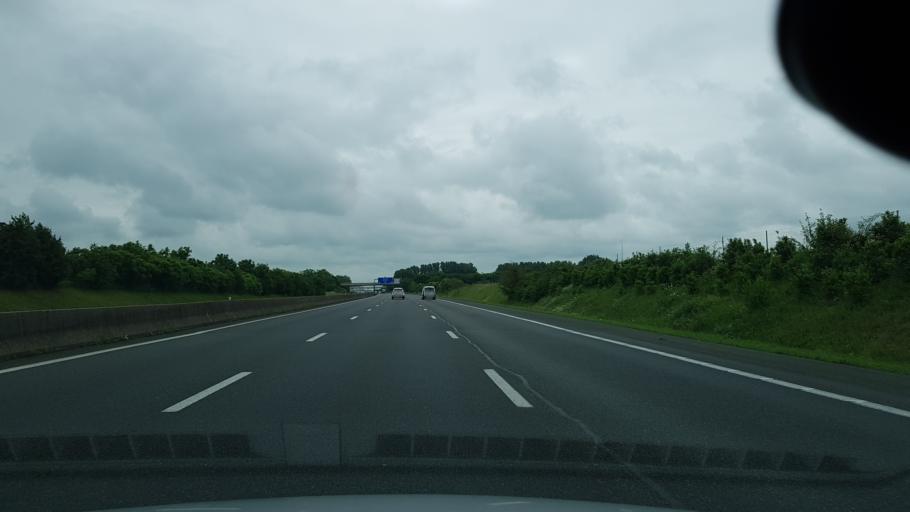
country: FR
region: Centre
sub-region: Departement d'Eure-et-Loir
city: Janville
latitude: 48.2112
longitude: 1.8473
